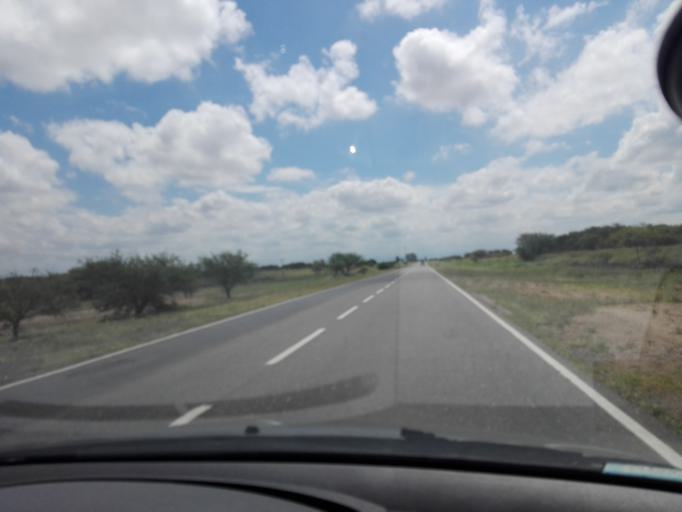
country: AR
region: Cordoba
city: Toledo
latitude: -31.6470
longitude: -64.0652
